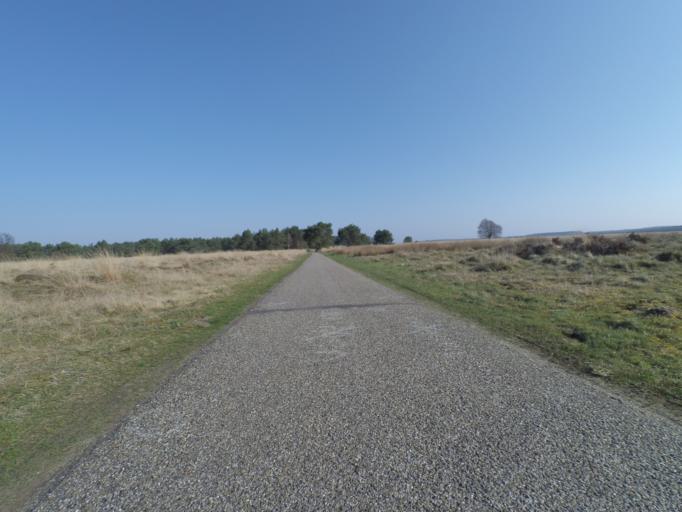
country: NL
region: Gelderland
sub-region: Gemeente Arnhem
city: Hoogkamp
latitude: 52.0752
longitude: 5.8632
